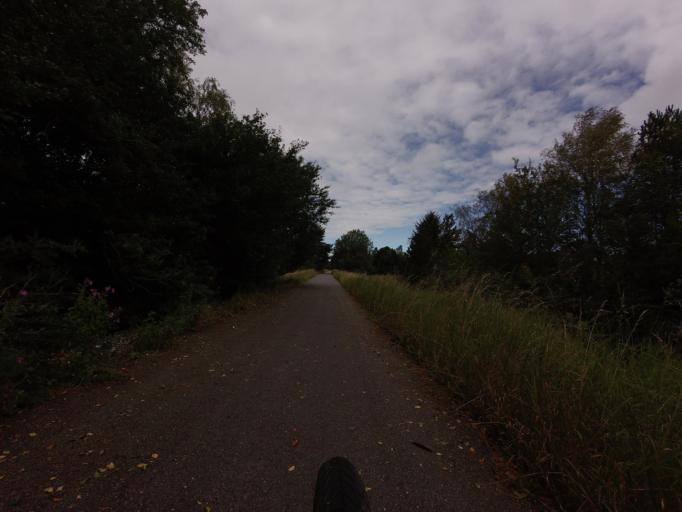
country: DK
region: Central Jutland
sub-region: Norddjurs Kommune
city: Auning
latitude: 56.3917
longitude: 10.4106
